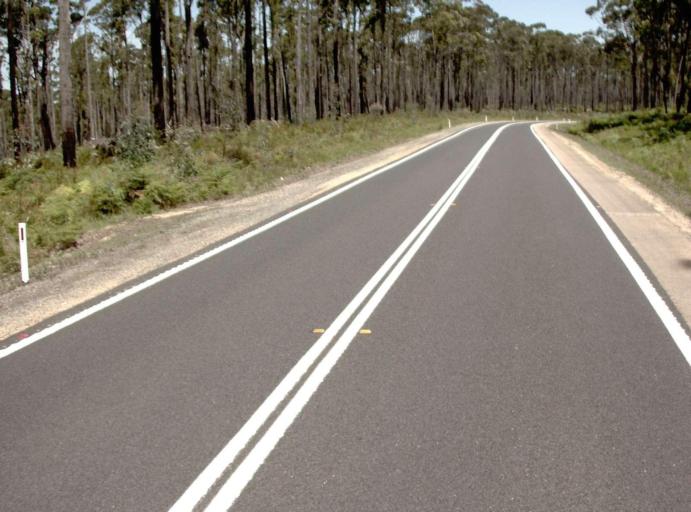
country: AU
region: Victoria
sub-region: East Gippsland
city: Lakes Entrance
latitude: -37.6652
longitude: 148.7998
